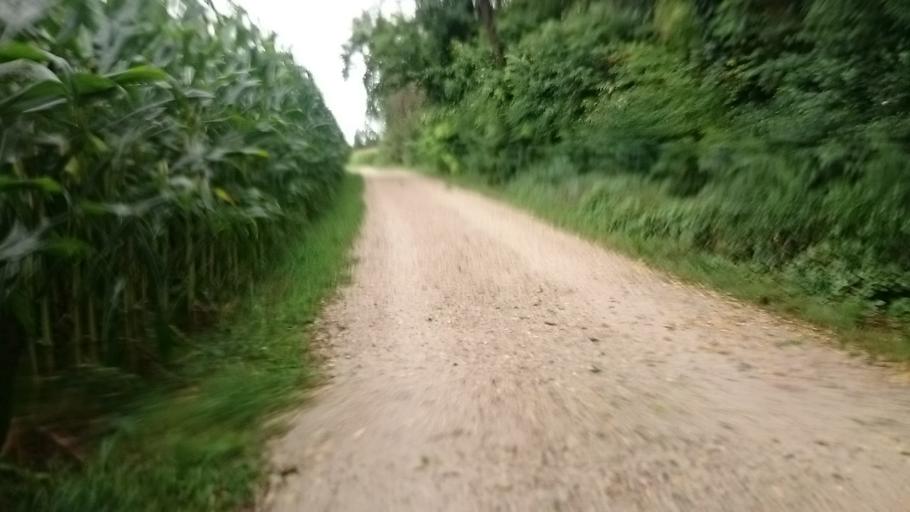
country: IT
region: Veneto
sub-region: Provincia di Treviso
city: Villa d'Asolo
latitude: 45.7731
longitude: 11.8874
